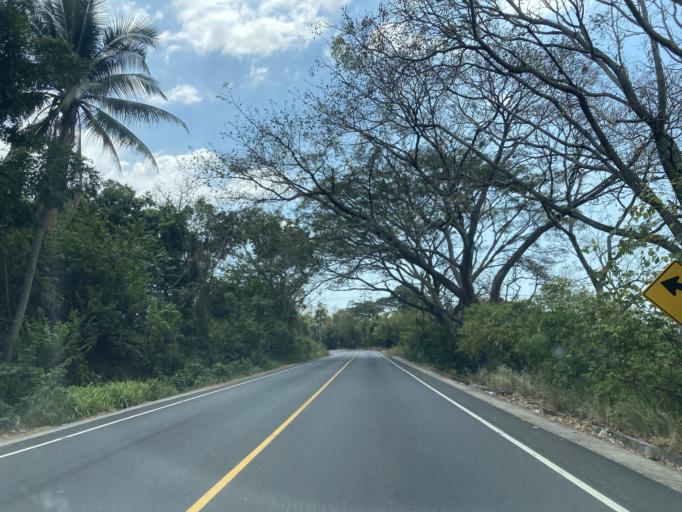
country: GT
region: Santa Rosa
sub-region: Municipio de Taxisco
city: Taxisco
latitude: 14.0677
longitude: -90.4713
